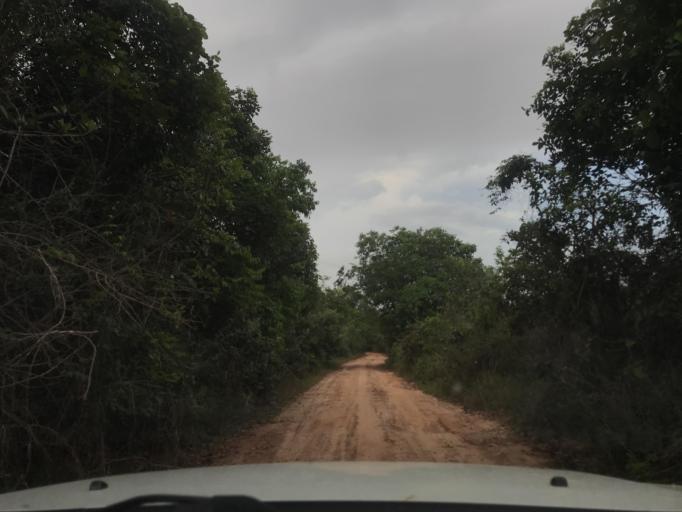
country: BR
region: Bahia
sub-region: Entre Rios
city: Entre Rios
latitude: -12.0509
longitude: -38.2279
